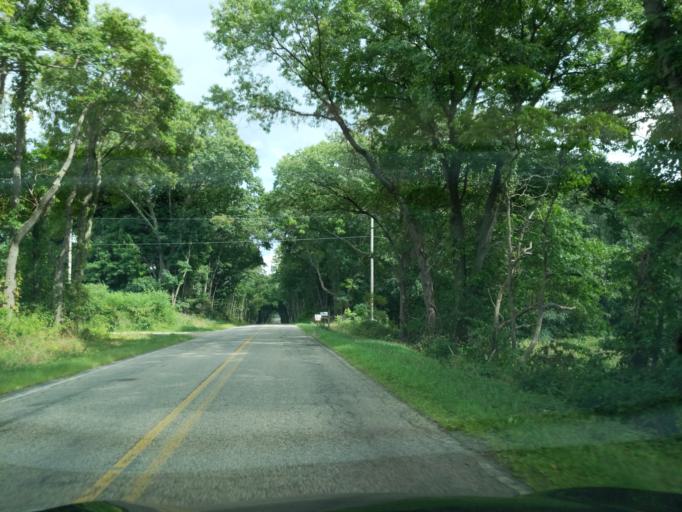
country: US
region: Michigan
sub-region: Eaton County
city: Eaton Rapids
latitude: 42.3787
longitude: -84.5792
